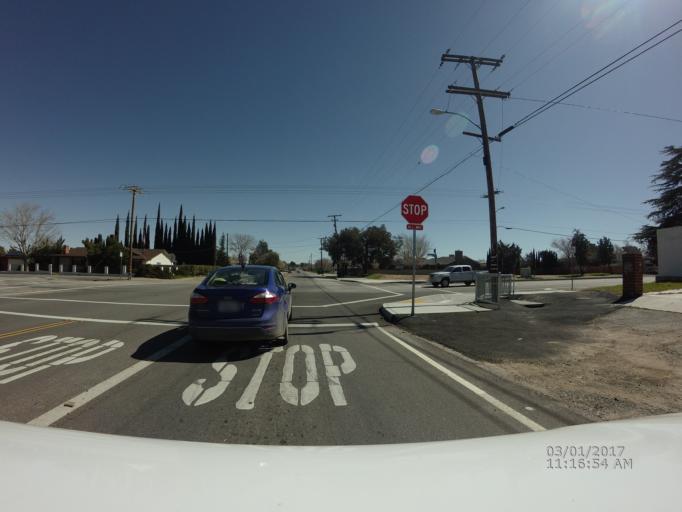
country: US
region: California
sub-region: Los Angeles County
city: Quartz Hill
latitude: 34.6456
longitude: -118.2274
